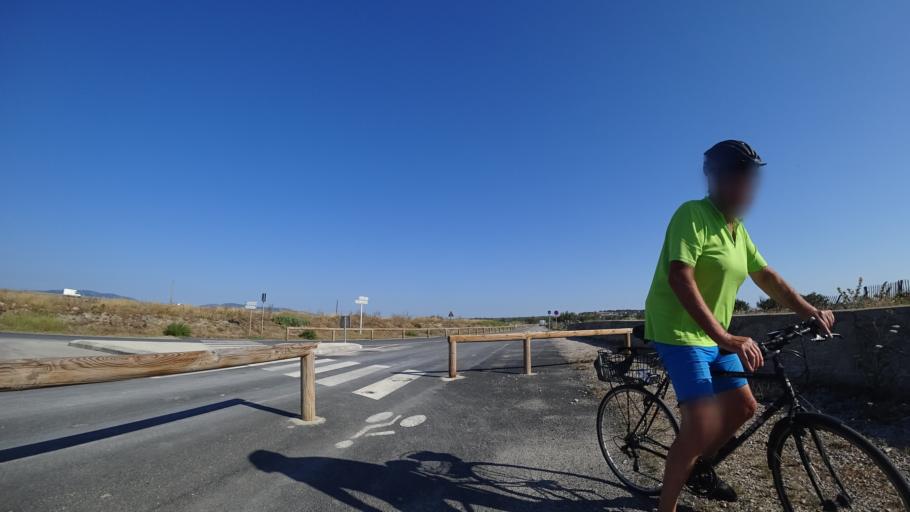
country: FR
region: Languedoc-Roussillon
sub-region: Departement de l'Aude
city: Leucate
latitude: 42.8868
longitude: 3.0505
